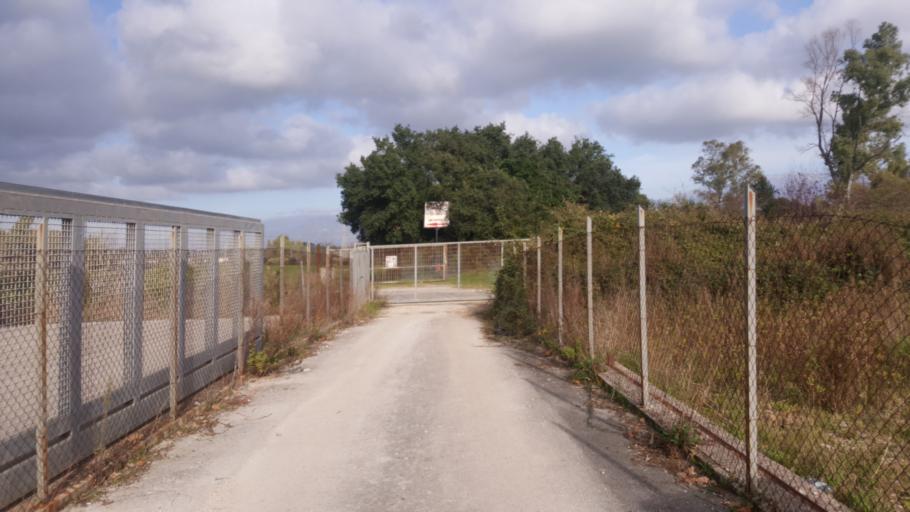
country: IT
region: Latium
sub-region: Provincia di Latina
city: Latina
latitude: 41.4764
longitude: 12.8862
